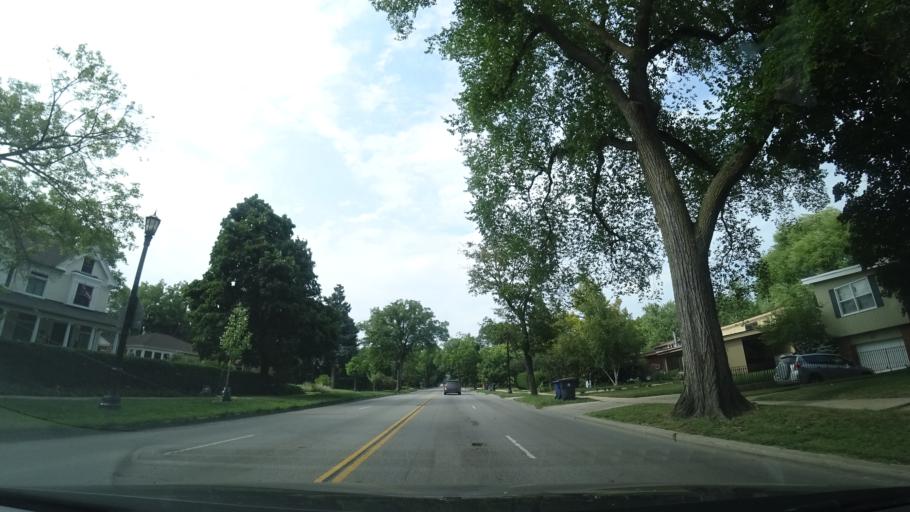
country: US
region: Illinois
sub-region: Cook County
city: Evanston
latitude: 42.0351
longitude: -87.6870
